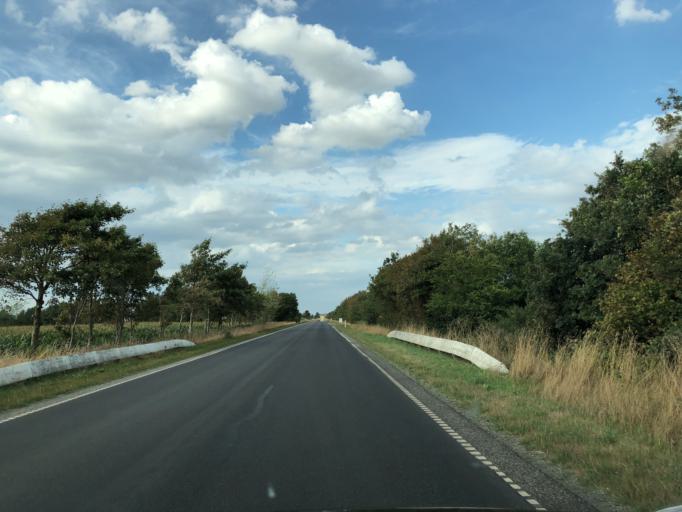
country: DK
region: Central Jutland
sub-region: Holstebro Kommune
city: Holstebro
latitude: 56.3815
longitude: 8.4499
